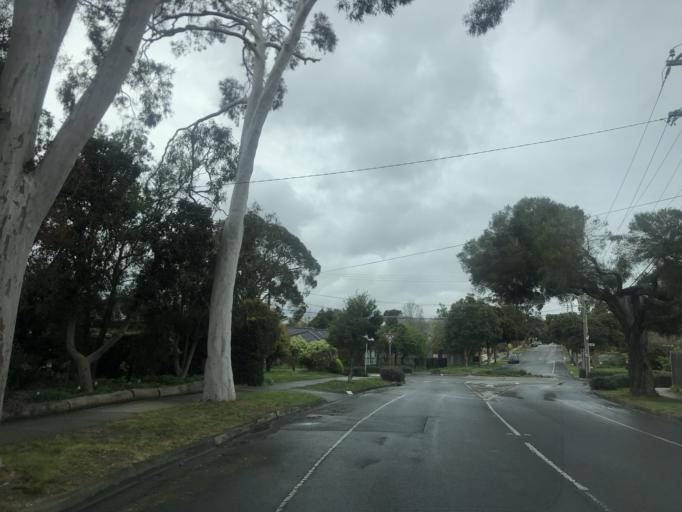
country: AU
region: Victoria
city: Burwood East
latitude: -37.8638
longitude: 145.1436
